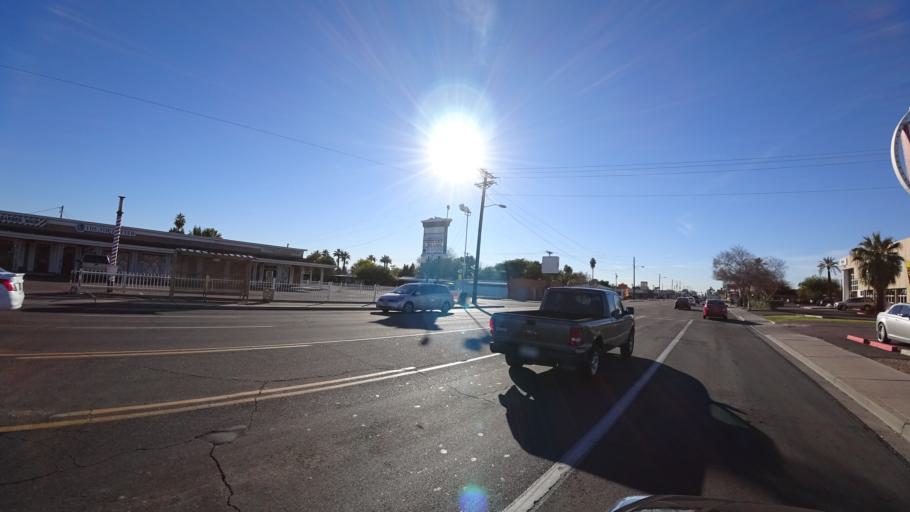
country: US
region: Arizona
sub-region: Maricopa County
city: Phoenix
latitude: 33.4805
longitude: -112.0082
